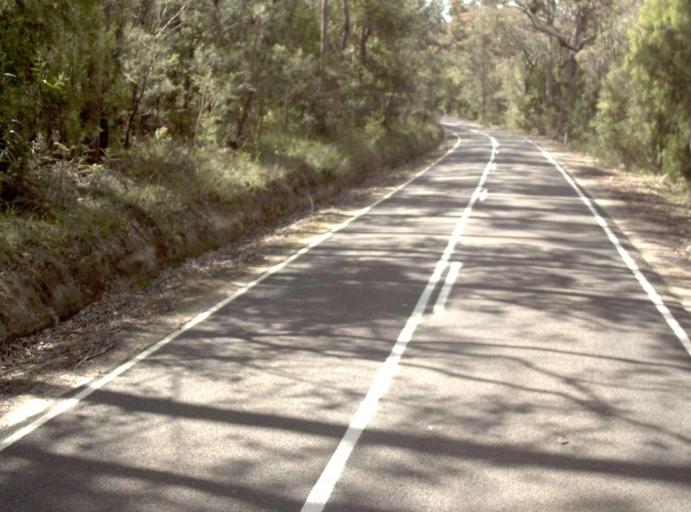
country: AU
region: New South Wales
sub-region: Bega Valley
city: Eden
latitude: -37.5257
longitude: 149.6892
